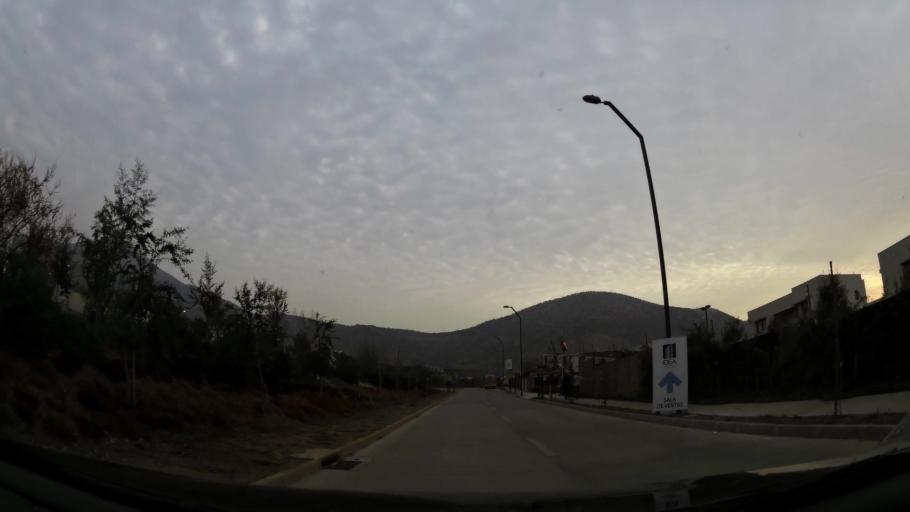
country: CL
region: Santiago Metropolitan
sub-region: Provincia de Chacabuco
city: Chicureo Abajo
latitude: -33.3207
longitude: -70.6467
